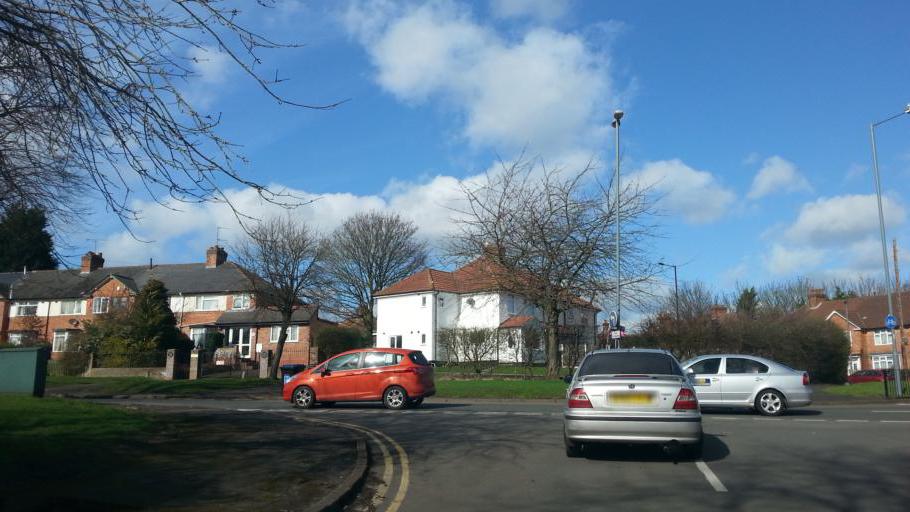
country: GB
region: England
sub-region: City and Borough of Birmingham
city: Bartley Green
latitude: 52.4482
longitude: -1.9482
